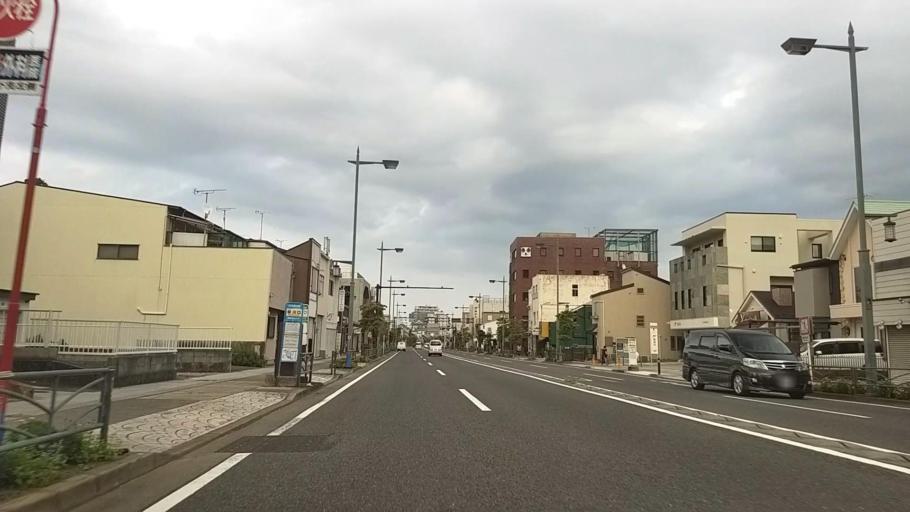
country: JP
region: Kanagawa
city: Odawara
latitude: 35.2467
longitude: 139.1505
